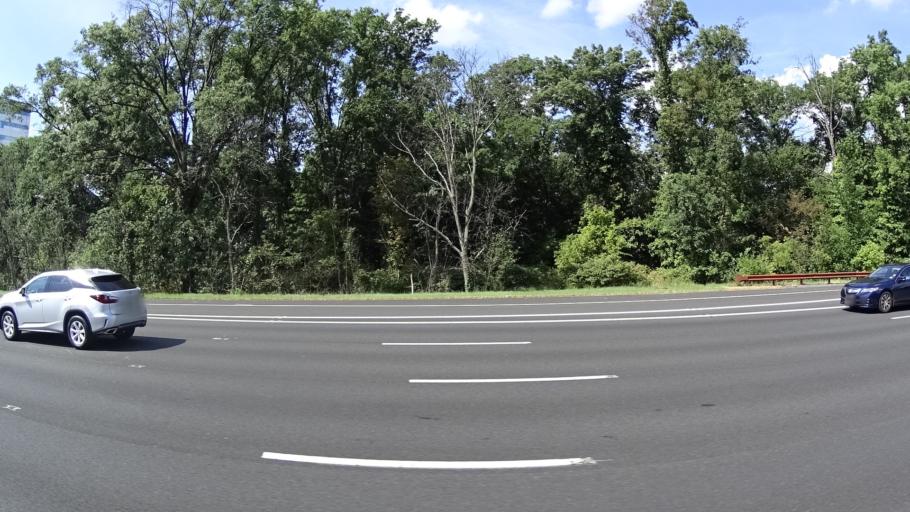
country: US
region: New Jersey
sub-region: Middlesex County
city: Iselin
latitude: 40.5668
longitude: -74.3253
